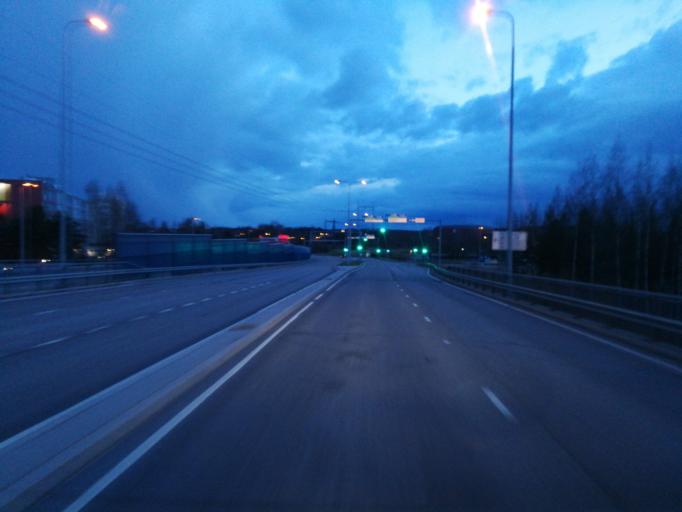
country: FI
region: Varsinais-Suomi
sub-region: Turku
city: Raisio
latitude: 60.4617
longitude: 22.1987
